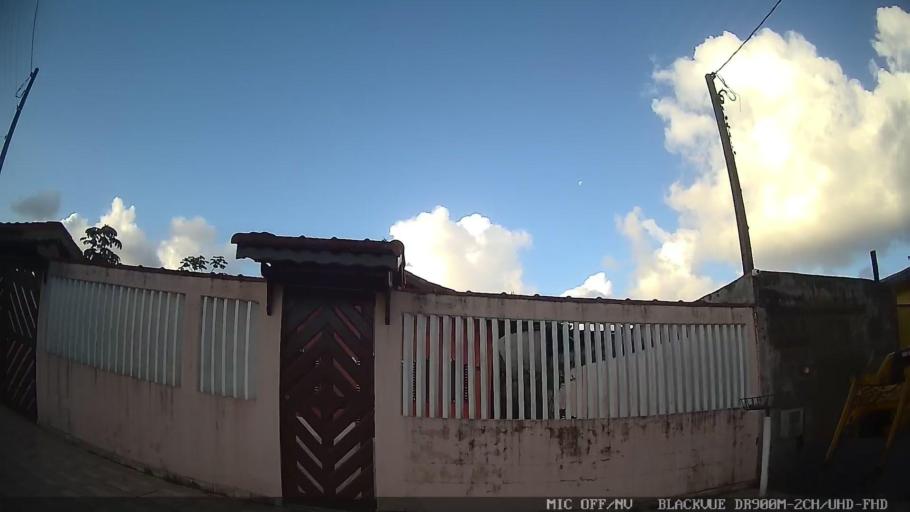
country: BR
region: Sao Paulo
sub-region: Itanhaem
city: Itanhaem
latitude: -24.1422
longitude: -46.7263
